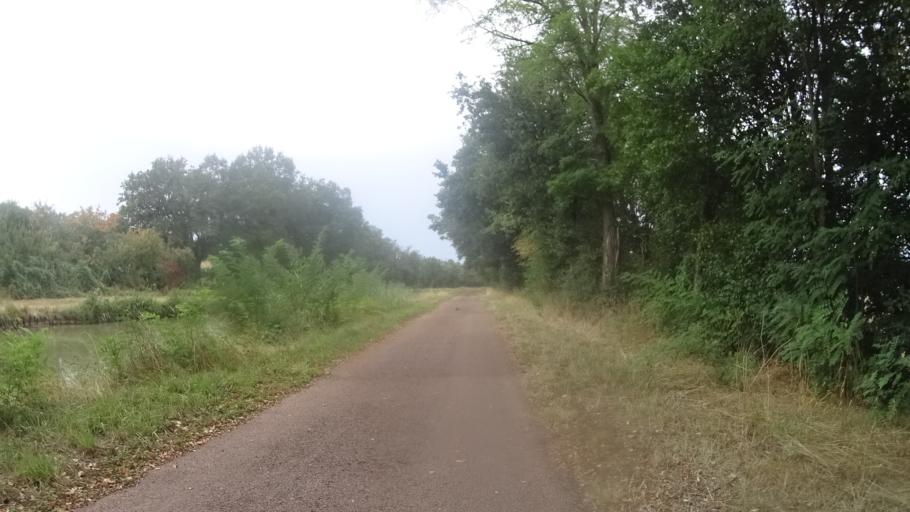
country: FR
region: Bourgogne
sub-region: Departement de la Nievre
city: Imphy
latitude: 46.8994
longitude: 3.2457
